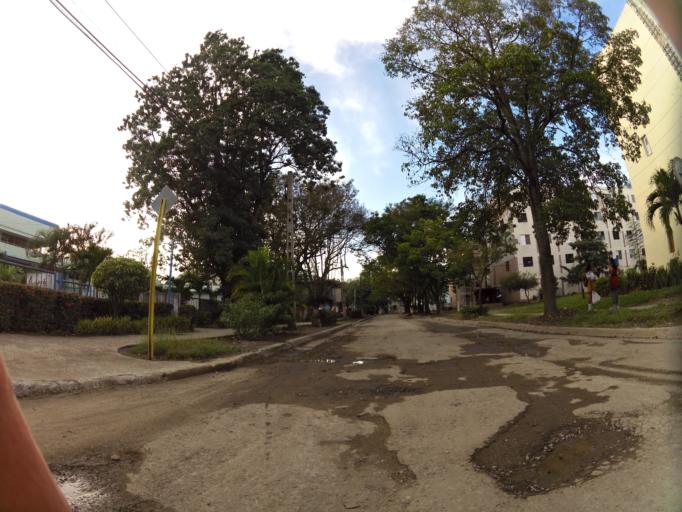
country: CU
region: Las Tunas
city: Las Tunas
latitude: 20.9670
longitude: -76.9336
